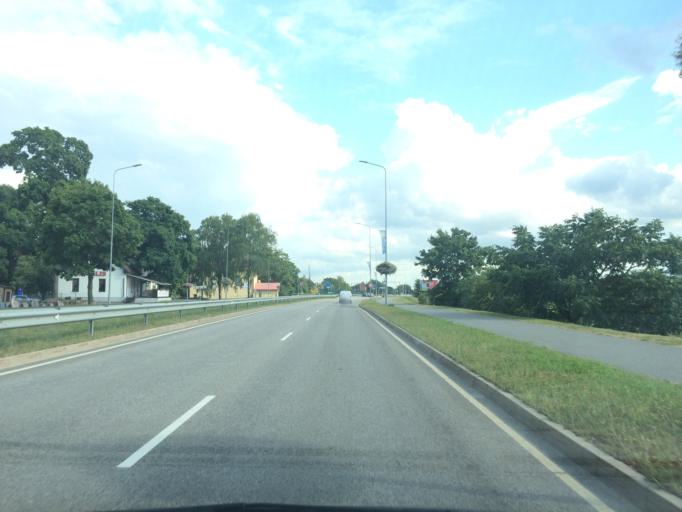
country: LV
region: Ogre
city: Ogre
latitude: 56.8132
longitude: 24.5962
